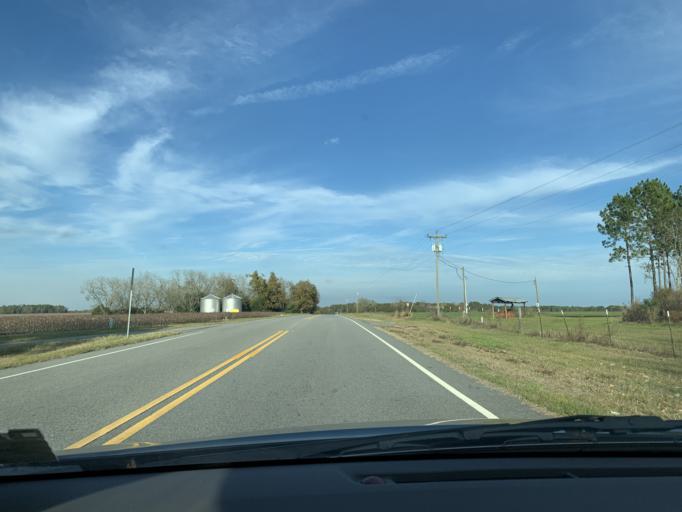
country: US
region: Georgia
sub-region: Irwin County
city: Ocilla
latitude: 31.6180
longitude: -83.4314
